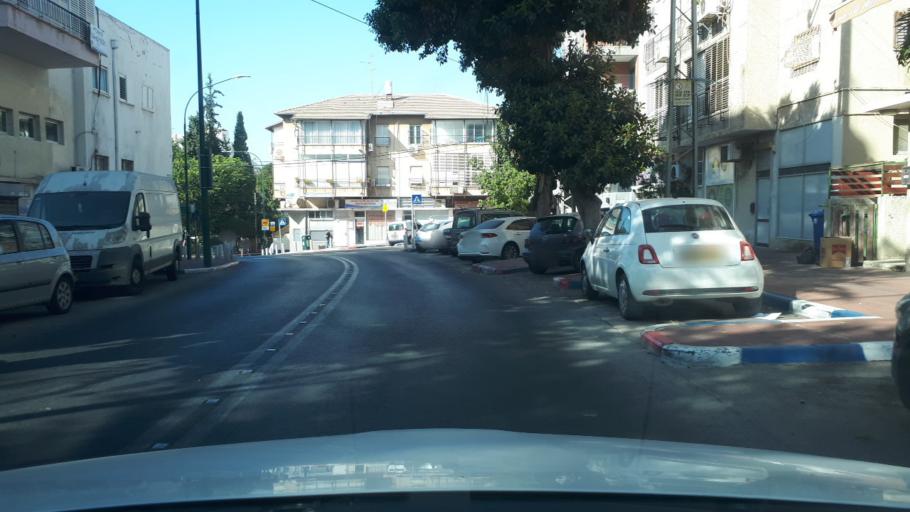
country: IL
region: Tel Aviv
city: Giv`atayim
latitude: 32.0730
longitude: 34.8233
